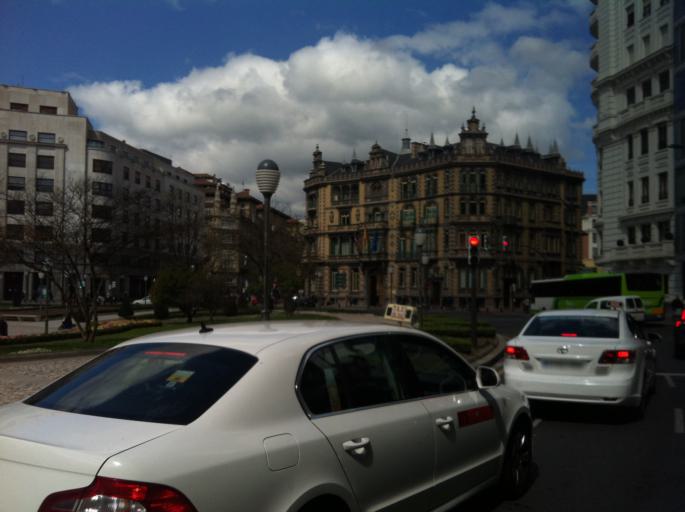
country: ES
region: Basque Country
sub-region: Bizkaia
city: Bilbao
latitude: 43.2632
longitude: -2.9346
